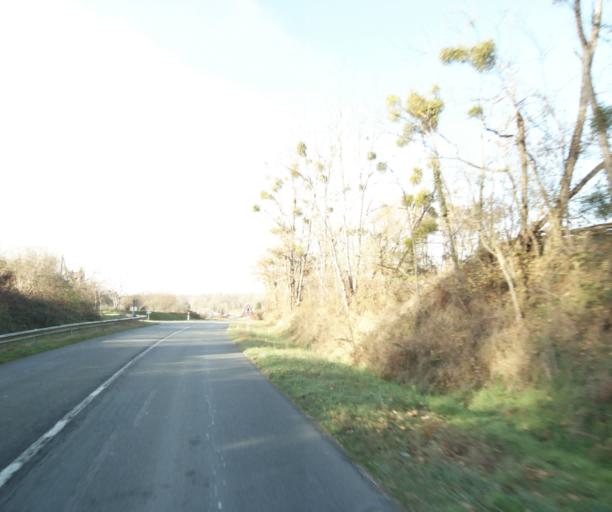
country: FR
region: Poitou-Charentes
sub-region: Departement de la Charente-Maritime
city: Burie
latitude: 45.7933
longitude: -0.4393
